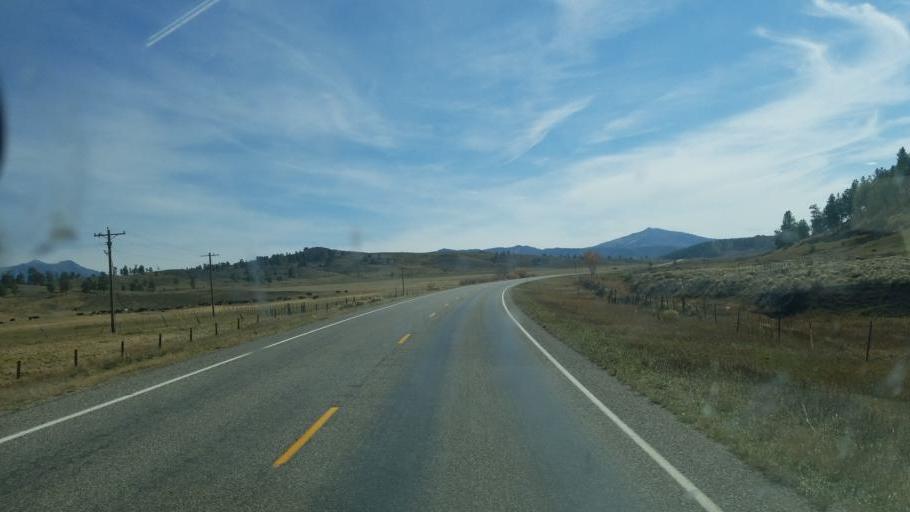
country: US
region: New Mexico
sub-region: Rio Arriba County
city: Dulce
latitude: 37.0333
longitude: -106.8322
